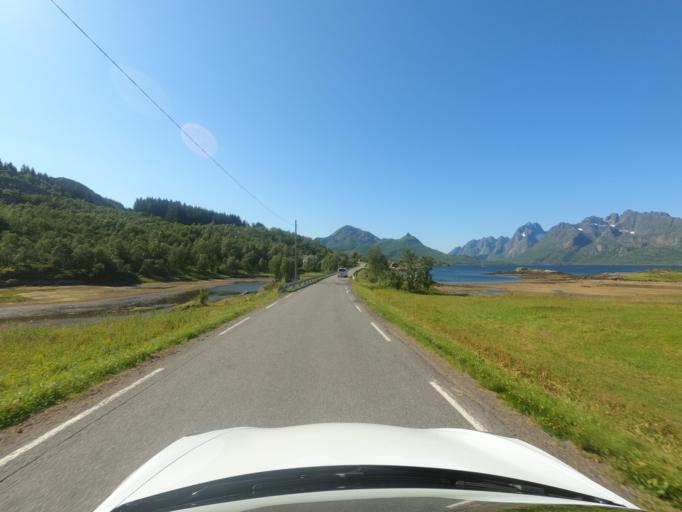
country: NO
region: Nordland
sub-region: Hadsel
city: Stokmarknes
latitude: 68.3198
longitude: 15.0025
